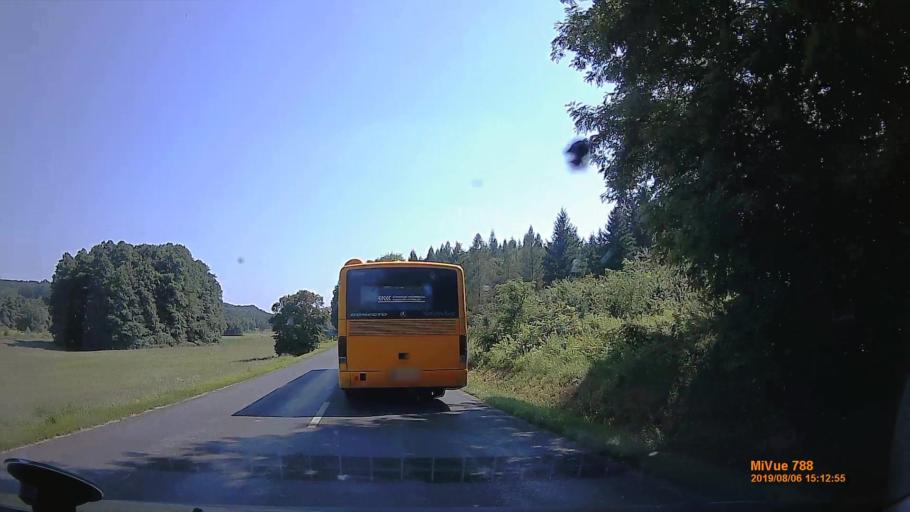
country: HU
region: Zala
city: Nagykanizsa
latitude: 46.3610
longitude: 16.9767
